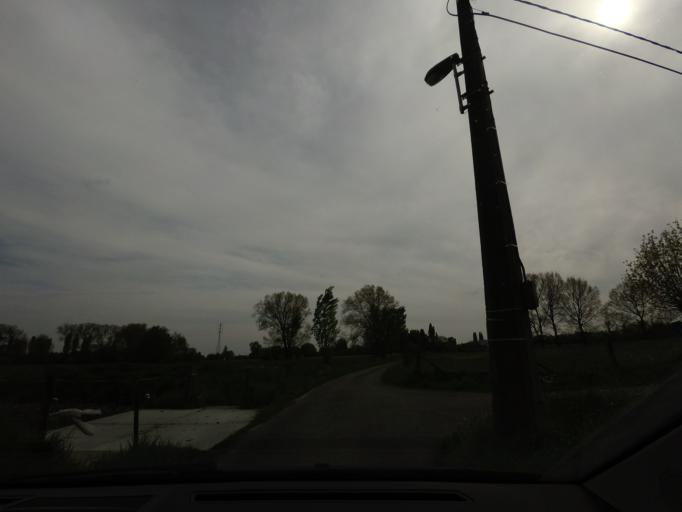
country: BE
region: Flanders
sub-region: Provincie Antwerpen
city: Lint
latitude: 51.1036
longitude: 4.4784
